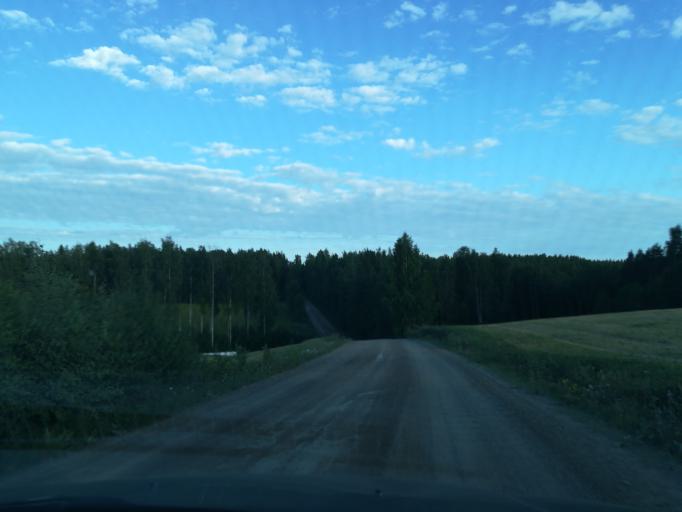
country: FI
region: Southern Savonia
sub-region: Mikkeli
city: Puumala
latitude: 61.5887
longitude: 28.1164
